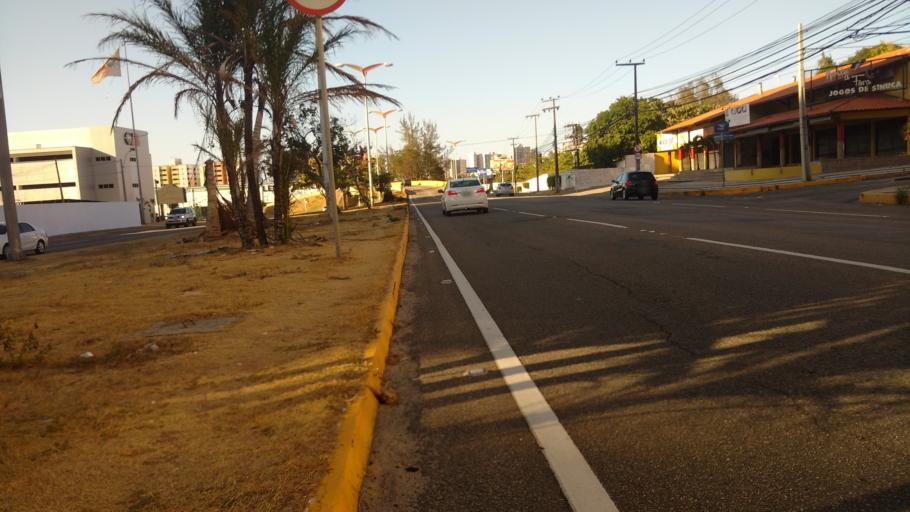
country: BR
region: Ceara
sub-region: Fortaleza
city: Fortaleza
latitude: -3.7612
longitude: -38.4829
